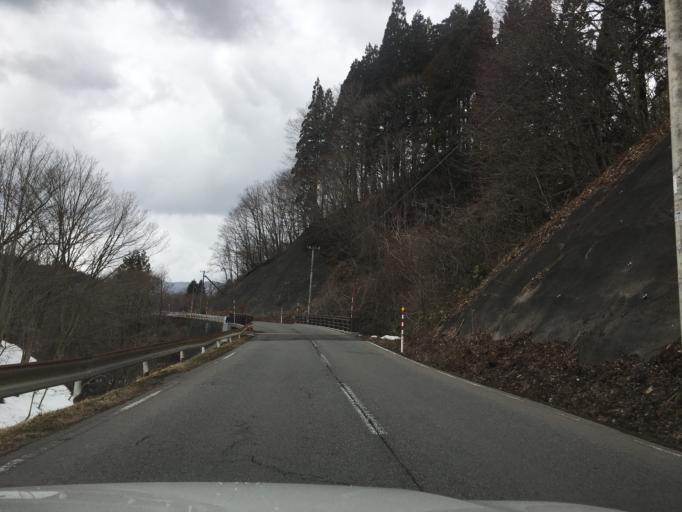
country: JP
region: Akita
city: Odate
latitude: 40.4260
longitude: 140.6553
